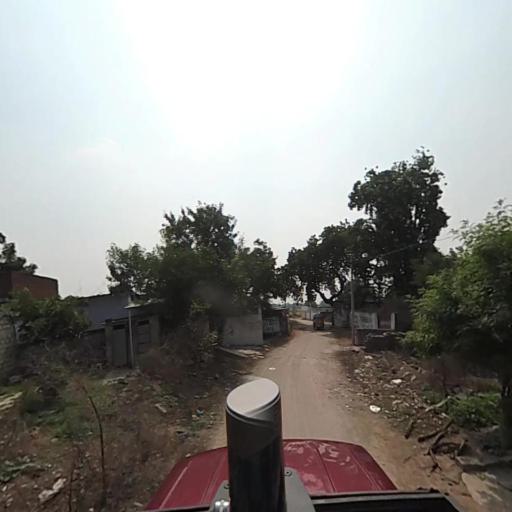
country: IN
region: Telangana
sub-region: Nalgonda
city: Nalgonda
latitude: 17.1856
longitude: 79.1261
